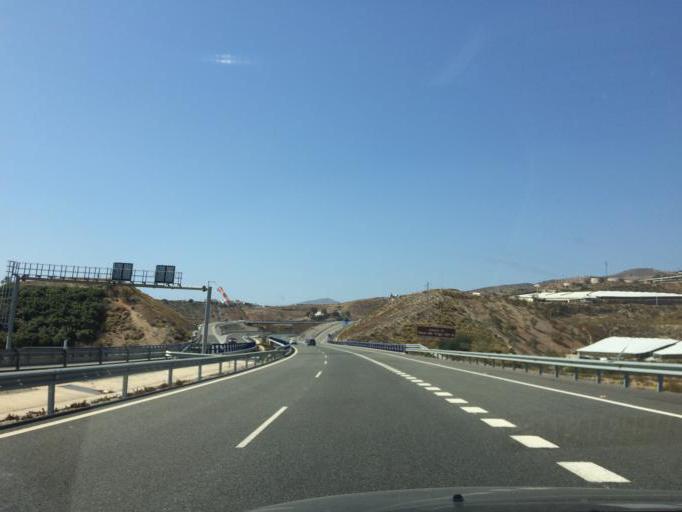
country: ES
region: Andalusia
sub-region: Provincia de Granada
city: Polopos
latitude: 36.7506
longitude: -3.3076
